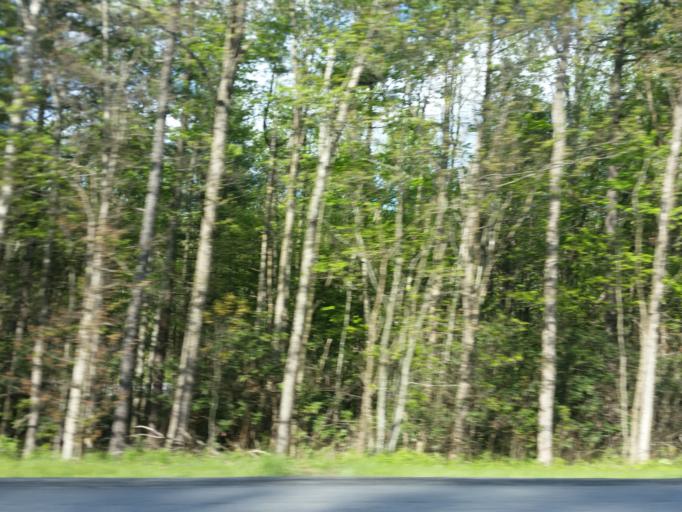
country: US
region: West Virginia
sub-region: Raleigh County
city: Shady Spring
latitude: 37.6731
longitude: -81.1160
